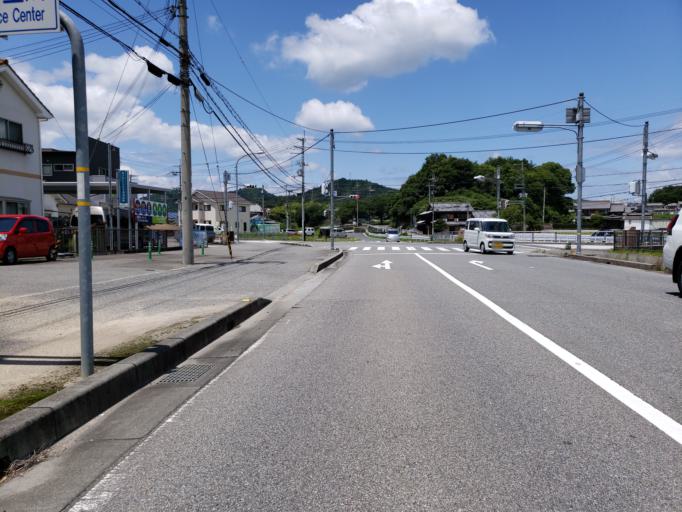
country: JP
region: Hyogo
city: Himeji
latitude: 34.9310
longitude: 134.7281
